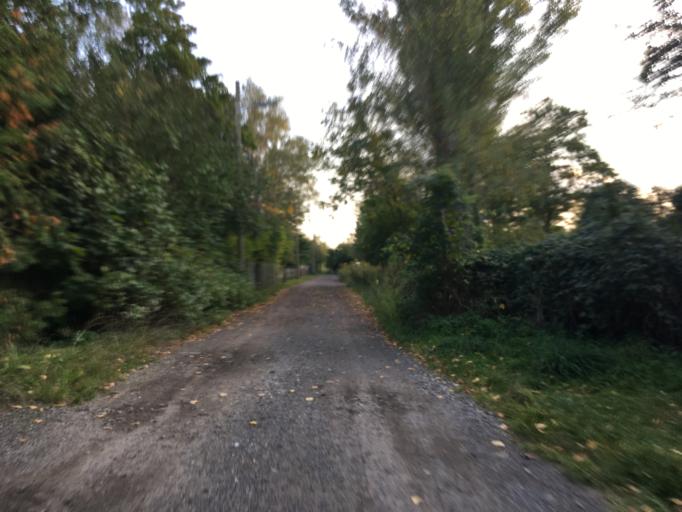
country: DE
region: Berlin
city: Biesdorf
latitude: 52.4889
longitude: 13.5520
